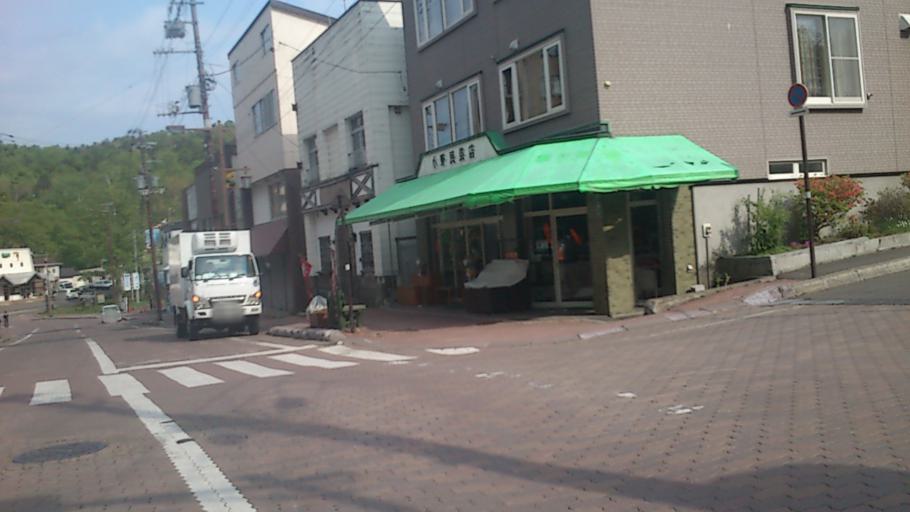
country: JP
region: Hokkaido
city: Bihoro
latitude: 43.4330
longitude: 144.0968
